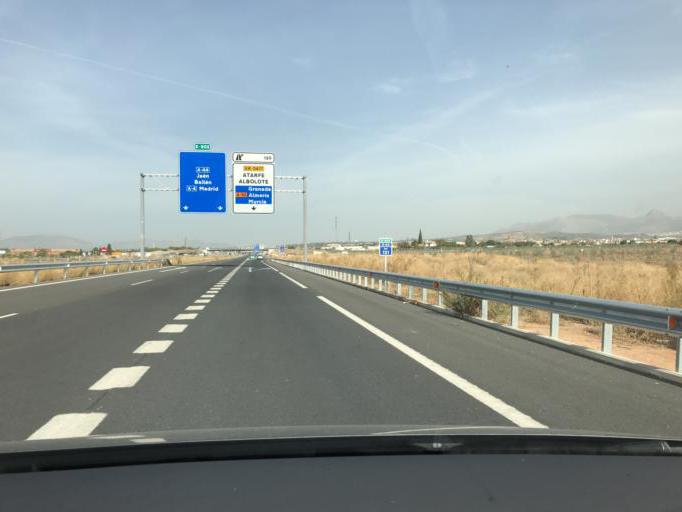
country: ES
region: Andalusia
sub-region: Provincia de Granada
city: Atarfe
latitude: 37.2206
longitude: -3.6698
